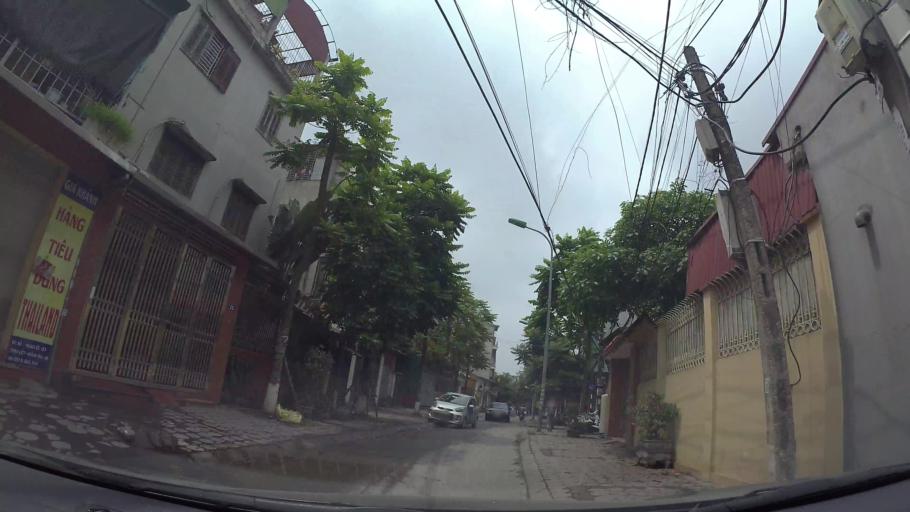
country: VN
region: Ha Noi
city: Van Dien
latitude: 20.9747
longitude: 105.8490
